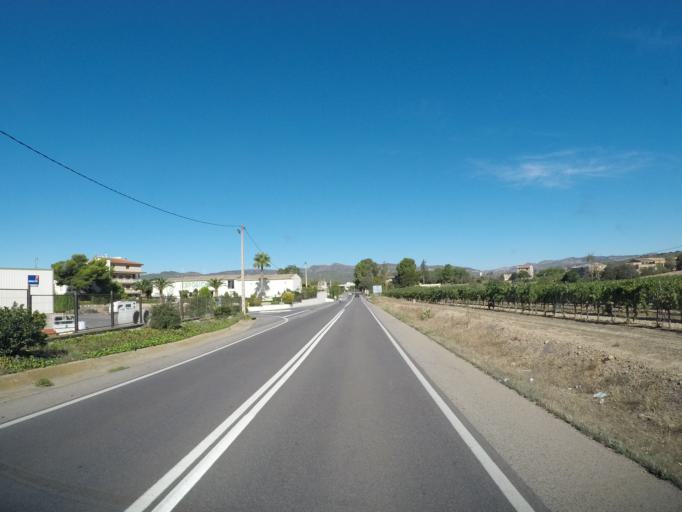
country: ES
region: Catalonia
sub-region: Provincia de Tarragona
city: Garcia
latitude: 41.0913
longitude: 0.6551
